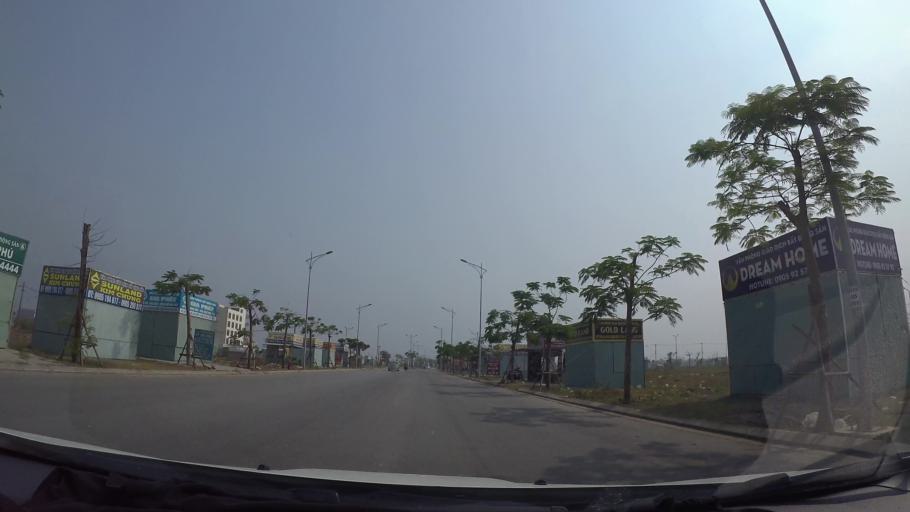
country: VN
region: Da Nang
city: Ngu Hanh Son
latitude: 16.0090
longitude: 108.2417
